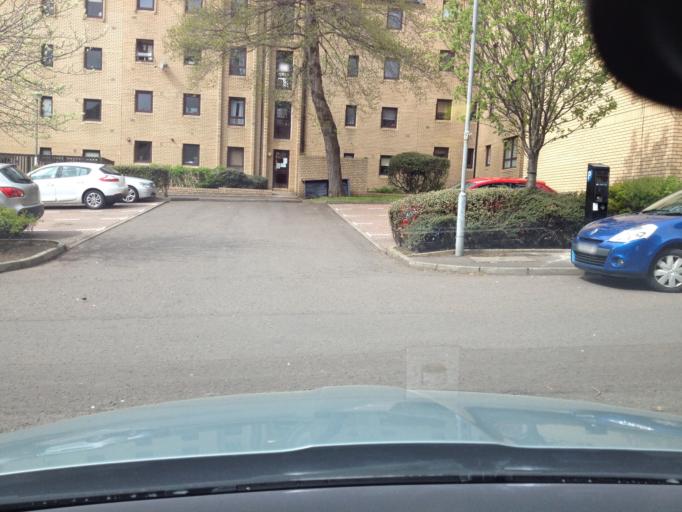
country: GB
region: Scotland
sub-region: Glasgow City
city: Glasgow
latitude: 55.8656
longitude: -4.2924
